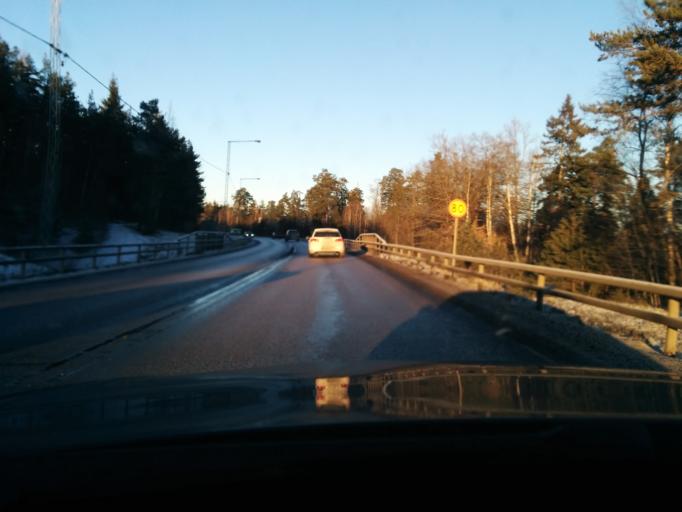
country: SE
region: Stockholm
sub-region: Taby Kommun
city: Taby
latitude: 59.4756
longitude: 18.1209
